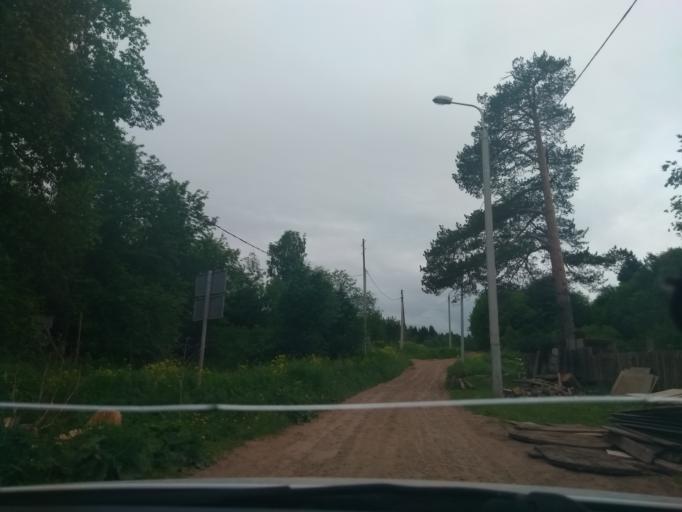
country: RU
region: Perm
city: Perm
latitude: 57.9897
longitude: 56.3375
